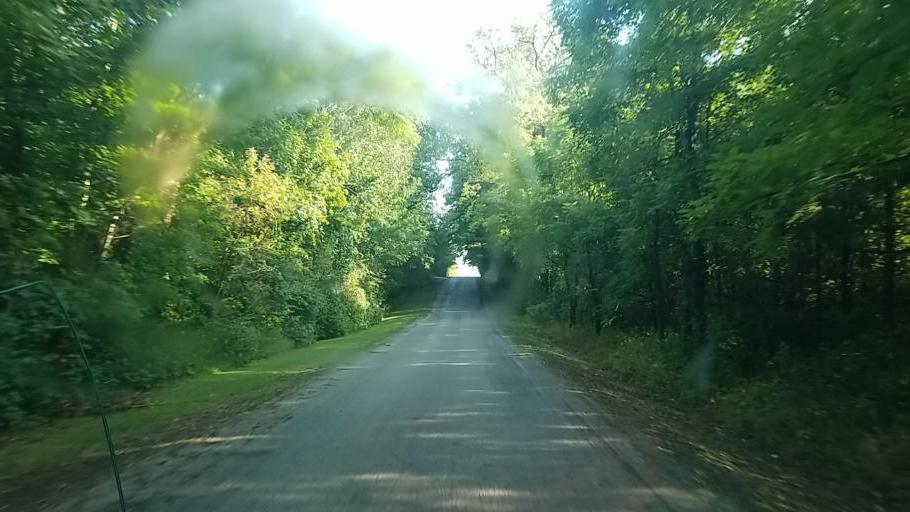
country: US
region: Ohio
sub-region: Crawford County
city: Bucyrus
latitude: 40.7677
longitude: -83.0551
